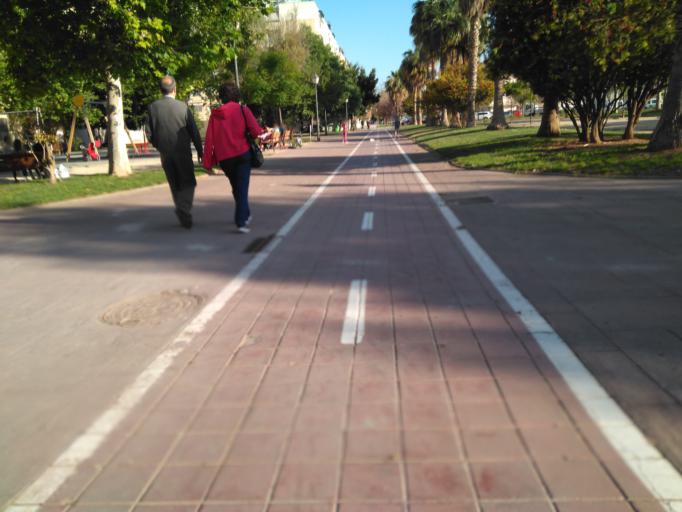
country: ES
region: Valencia
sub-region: Provincia de Valencia
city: Tavernes Blanques
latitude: 39.4959
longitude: -0.3857
